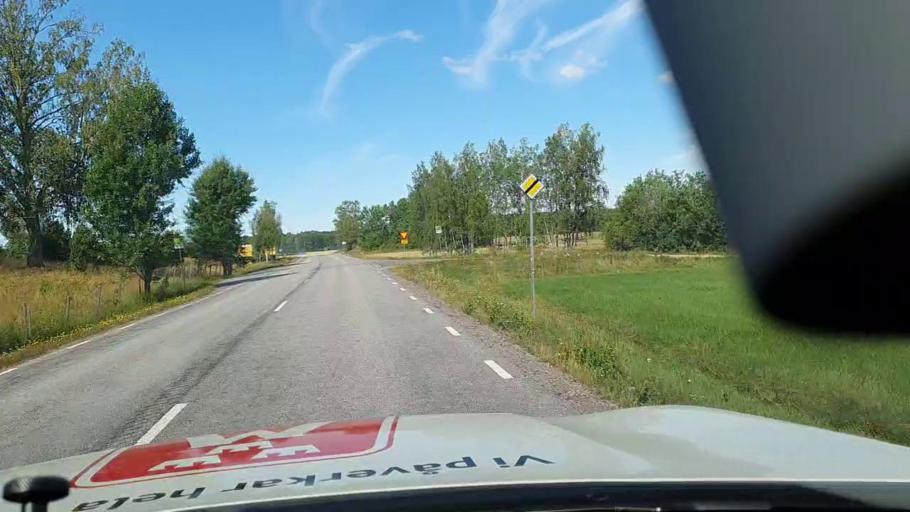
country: SE
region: Soedermanland
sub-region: Strangnas Kommun
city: Akers Styckebruk
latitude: 59.2722
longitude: 16.9755
